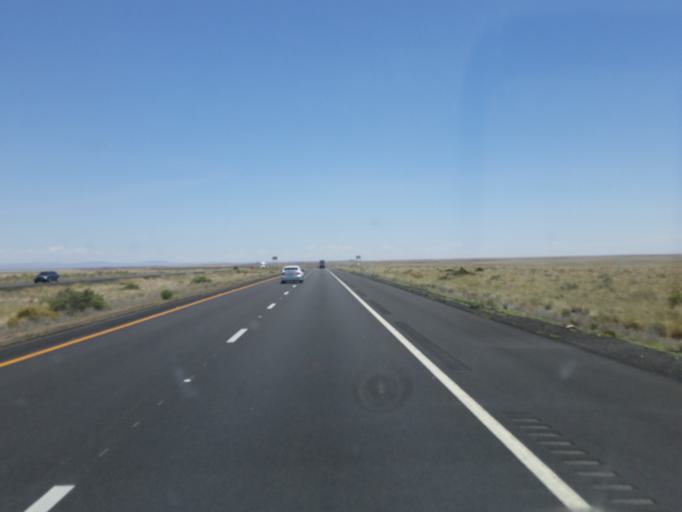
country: US
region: Arizona
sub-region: Coconino County
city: LeChee
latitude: 35.1179
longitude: -111.1284
